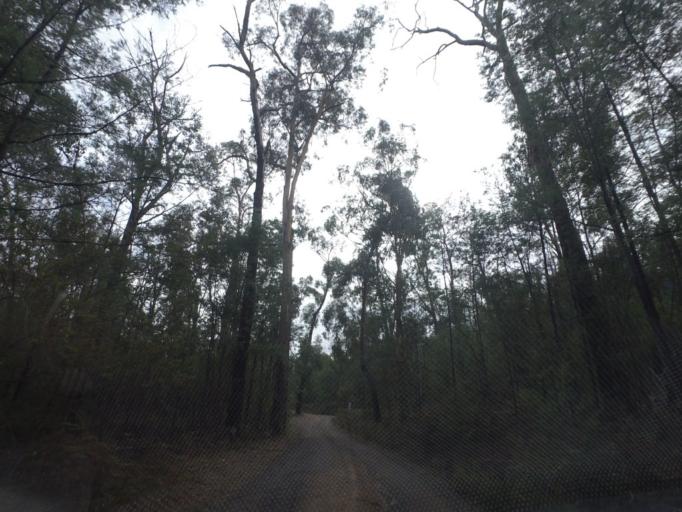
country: AU
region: Victoria
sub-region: Yarra Ranges
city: Healesville
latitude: -37.6318
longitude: 145.5360
